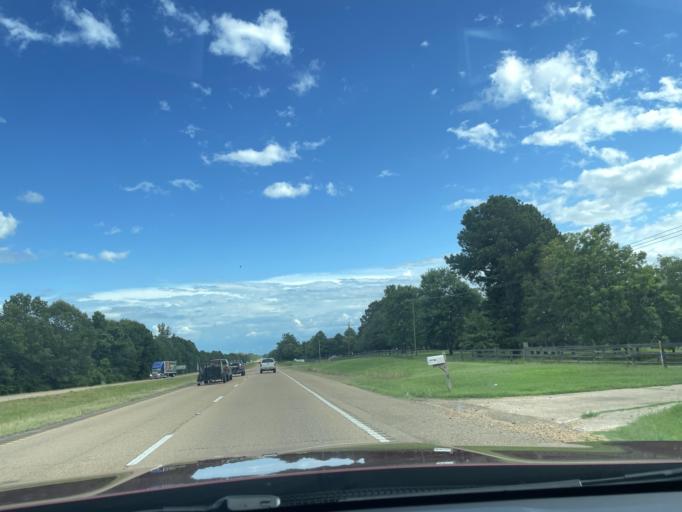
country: US
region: Mississippi
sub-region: Madison County
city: Flora
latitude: 32.5131
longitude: -90.3044
